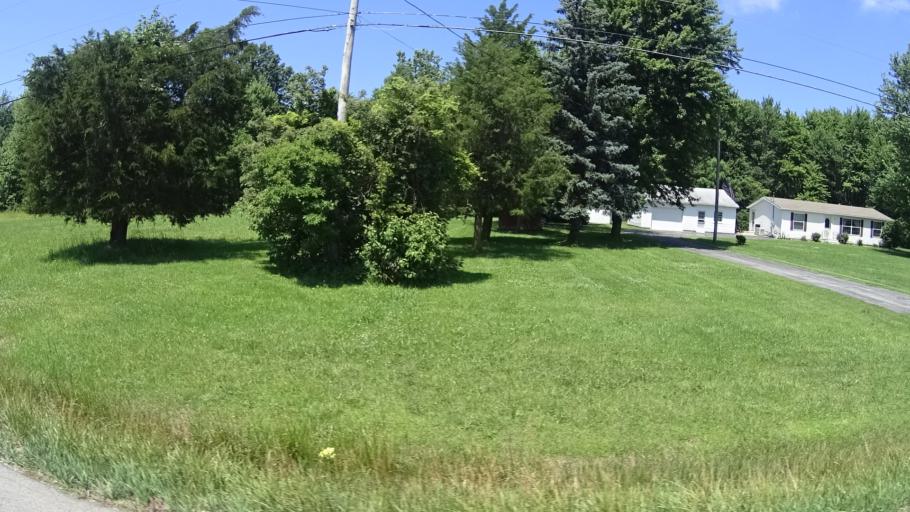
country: US
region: Ohio
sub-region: Huron County
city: Wakeman
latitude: 41.3267
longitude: -82.3893
